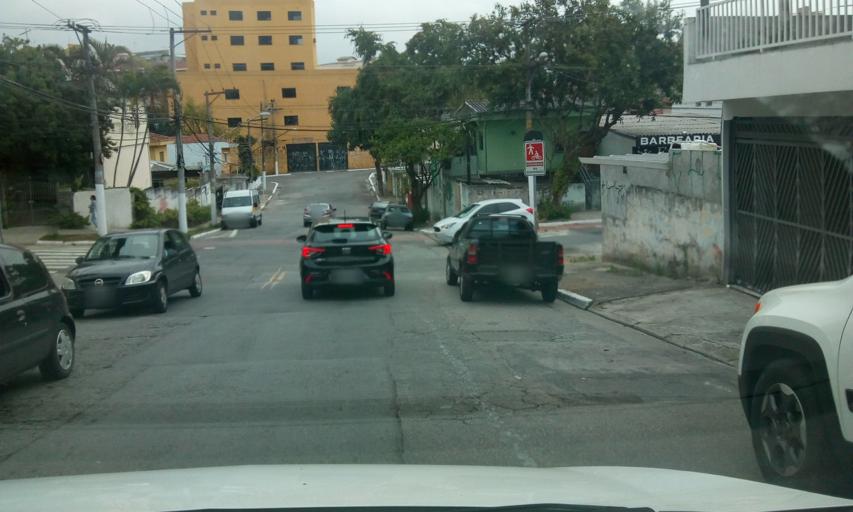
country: BR
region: Sao Paulo
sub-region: Sao Caetano Do Sul
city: Sao Caetano do Sul
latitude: -23.6187
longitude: -46.6077
